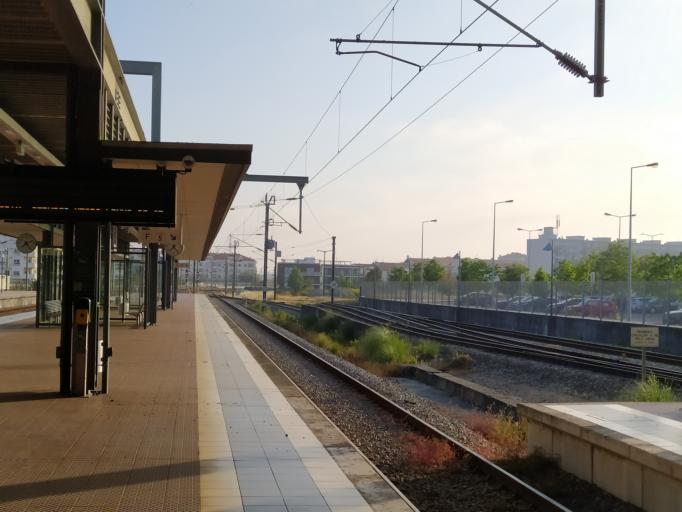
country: PT
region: Aveiro
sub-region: Aveiro
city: Aveiro
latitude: 40.6436
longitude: -8.6402
